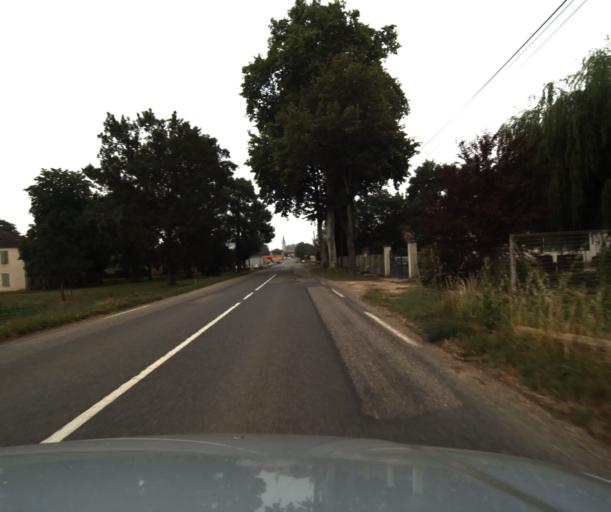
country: FR
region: Midi-Pyrenees
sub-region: Departement du Tarn-et-Garonne
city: Beaumont-de-Lomagne
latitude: 43.8093
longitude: 0.9006
